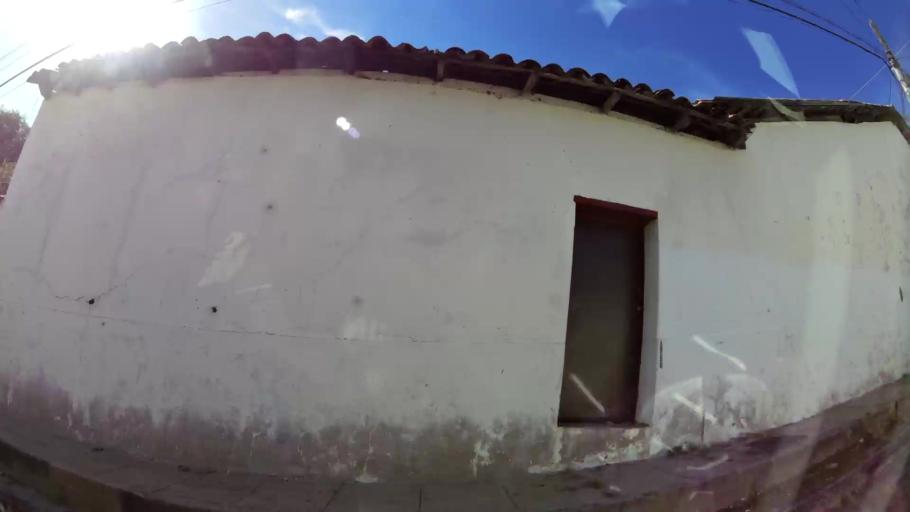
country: SV
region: Cuscatlan
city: Suchitoto
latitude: 13.9380
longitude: -89.0285
